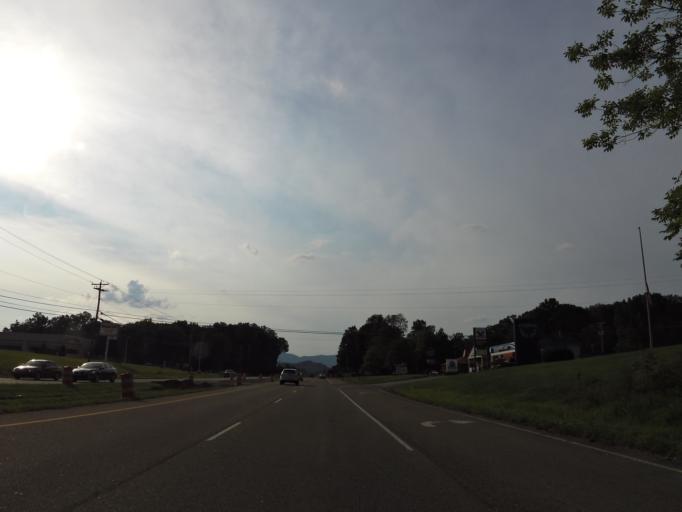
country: US
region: Tennessee
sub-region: Roane County
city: Oliver Springs
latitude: 36.0236
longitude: -84.3140
